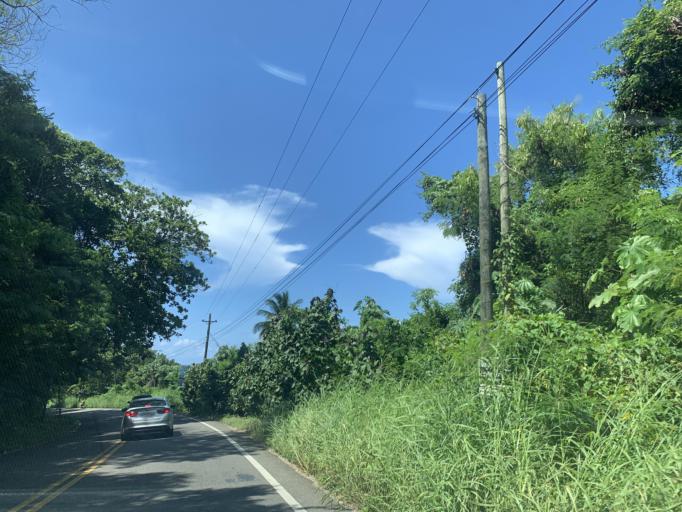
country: DO
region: Maria Trinidad Sanchez
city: Cabrera
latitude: 19.6540
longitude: -69.9340
